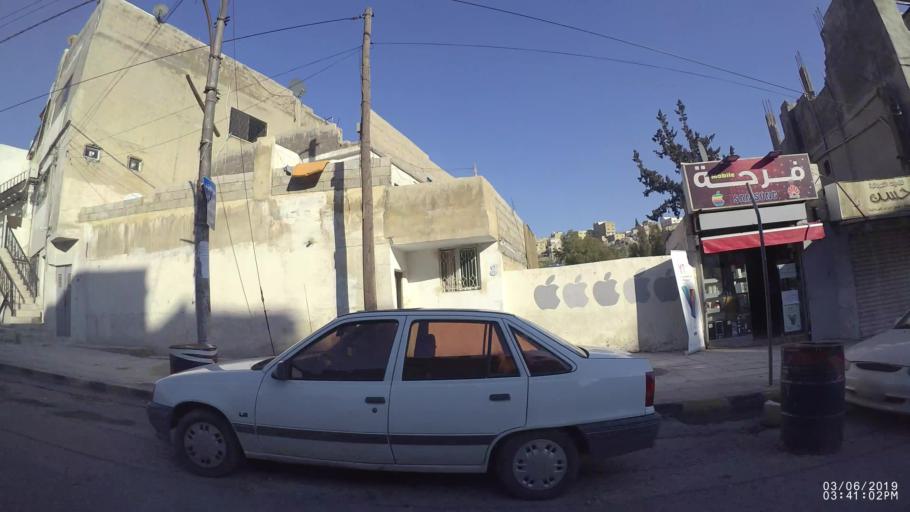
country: JO
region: Amman
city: Amman
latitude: 31.9634
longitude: 35.9590
